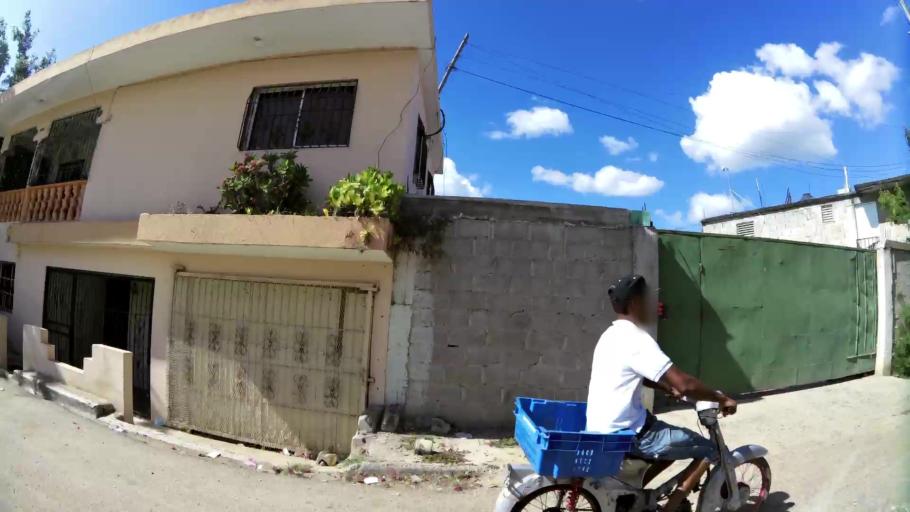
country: DO
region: Santo Domingo
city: Santo Domingo Oeste
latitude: 18.5444
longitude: -70.0385
